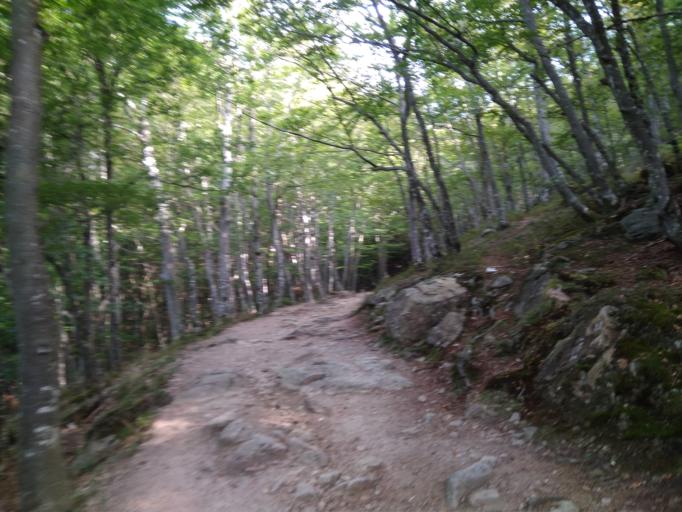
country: FR
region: Auvergne
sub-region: Departement de l'Allier
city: Le Mayet-de-Montagne
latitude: 46.1239
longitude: 3.7633
